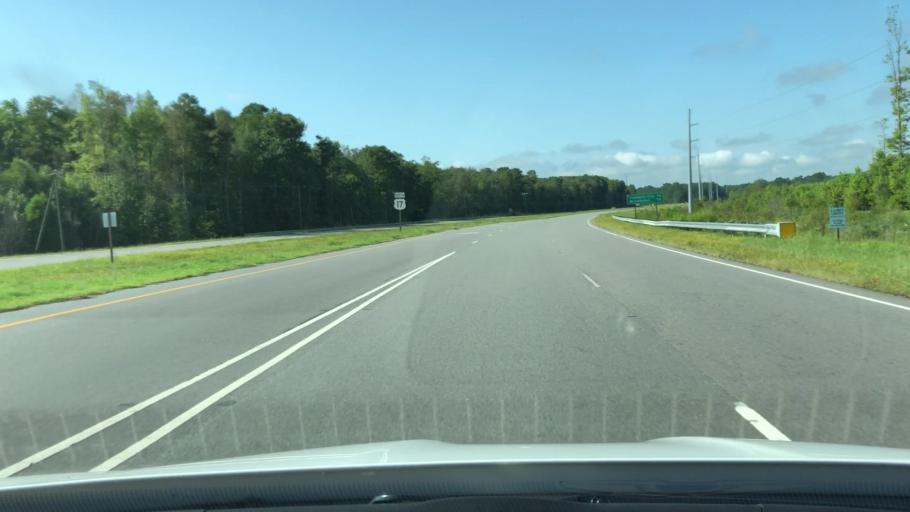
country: US
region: North Carolina
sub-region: Pasquotank County
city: Elizabeth City
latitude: 36.4351
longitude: -76.3389
